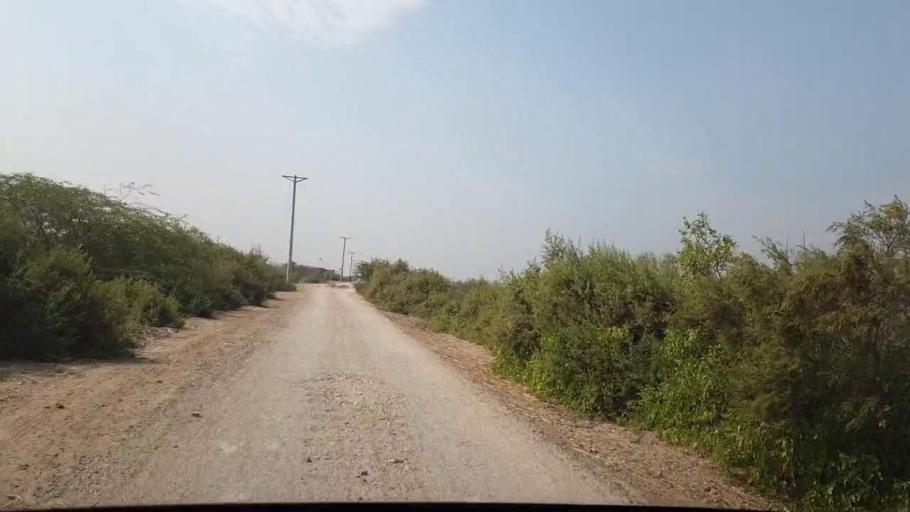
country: PK
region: Sindh
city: Chuhar Jamali
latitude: 24.2720
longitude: 67.9005
